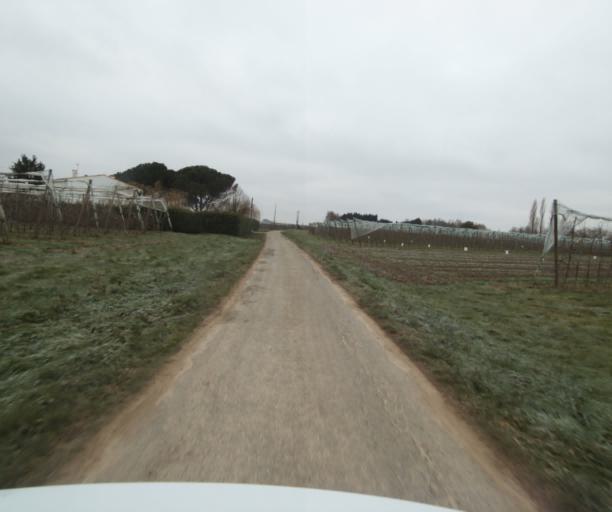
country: FR
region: Midi-Pyrenees
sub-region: Departement du Tarn-et-Garonne
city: Moissac
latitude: 44.1047
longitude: 1.1444
